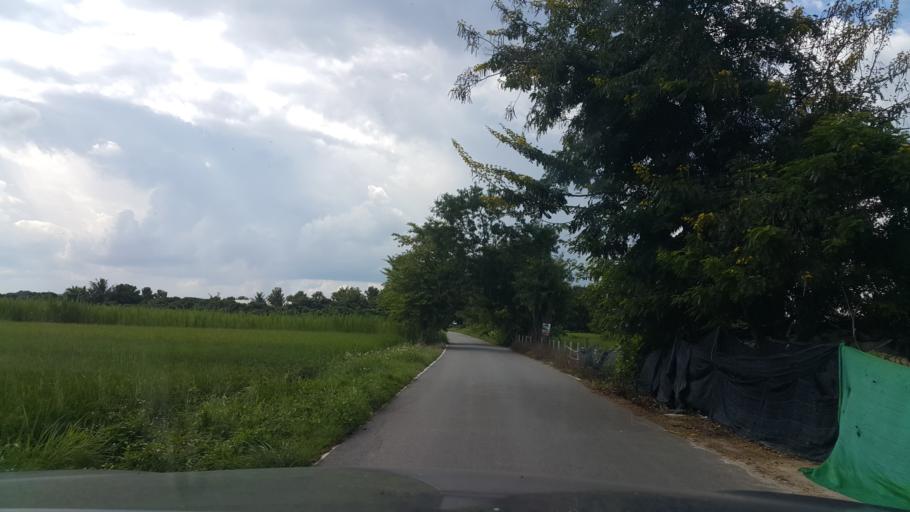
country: TH
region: Chiang Mai
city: San Kamphaeng
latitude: 18.7086
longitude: 99.1629
